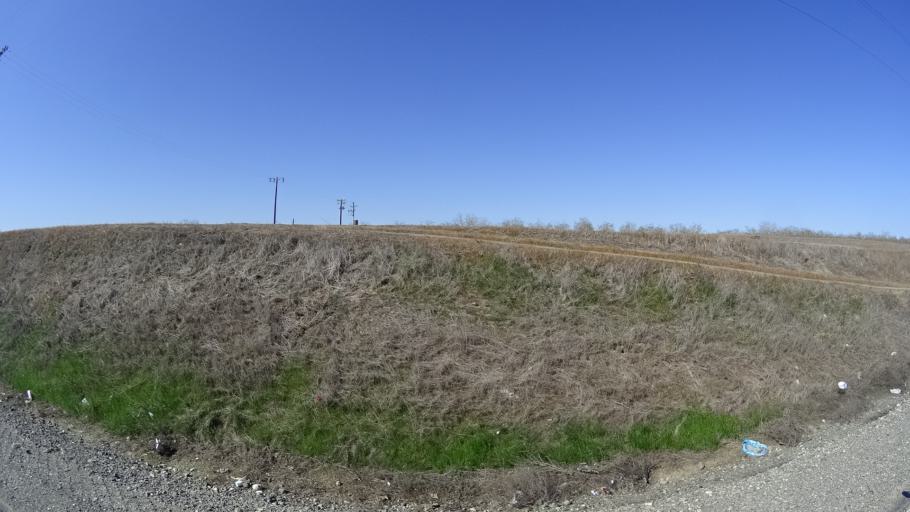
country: US
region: California
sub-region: Glenn County
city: Hamilton City
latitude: 39.7480
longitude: -122.0211
